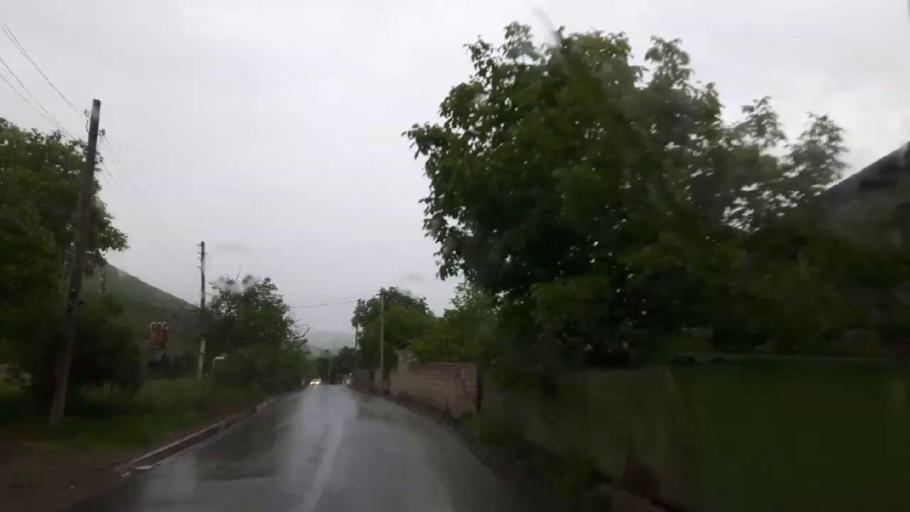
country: GE
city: Agara
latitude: 41.9818
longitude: 43.9383
